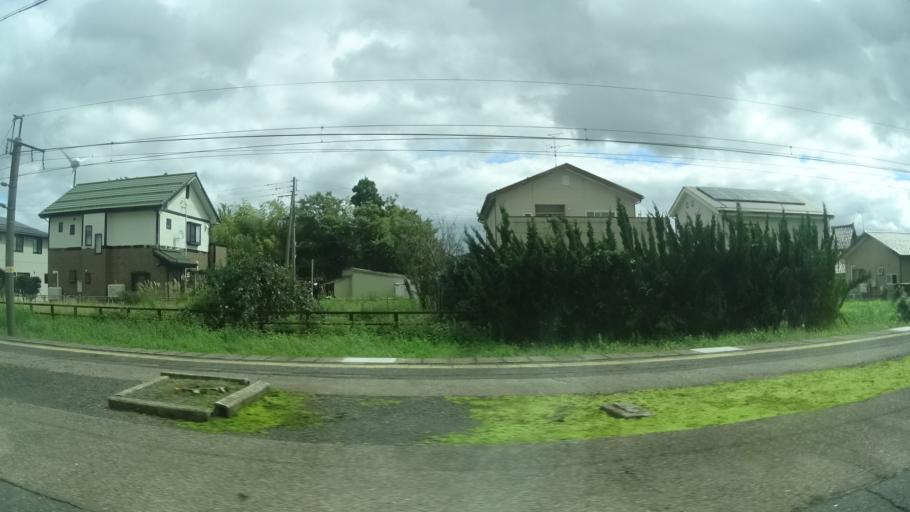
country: JP
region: Niigata
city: Shibata
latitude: 37.9763
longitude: 139.3583
